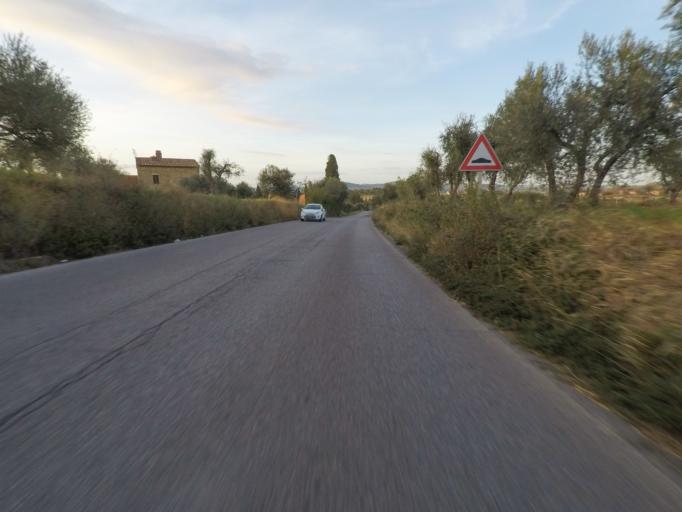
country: IT
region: Tuscany
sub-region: Provincia di Siena
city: Pienza
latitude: 43.0817
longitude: 11.6764
